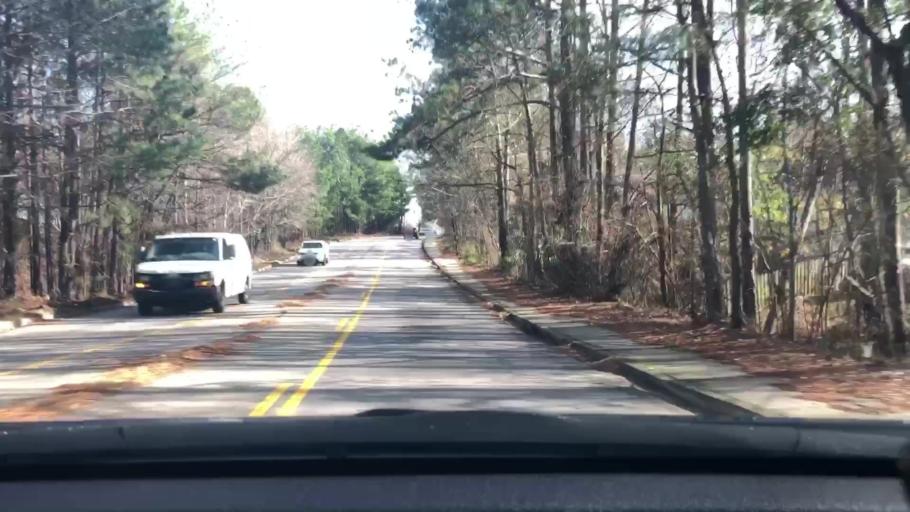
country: US
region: South Carolina
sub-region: Lexington County
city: Irmo
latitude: 34.0893
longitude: -81.1675
